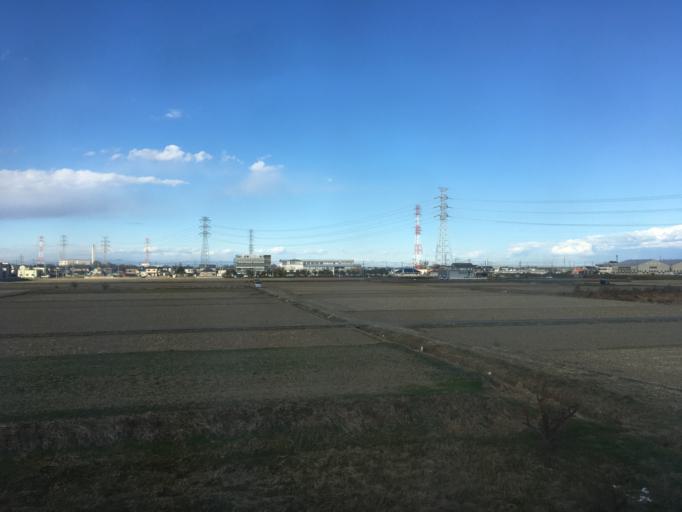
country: JP
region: Saitama
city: Kawagoe
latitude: 35.9226
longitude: 139.4575
